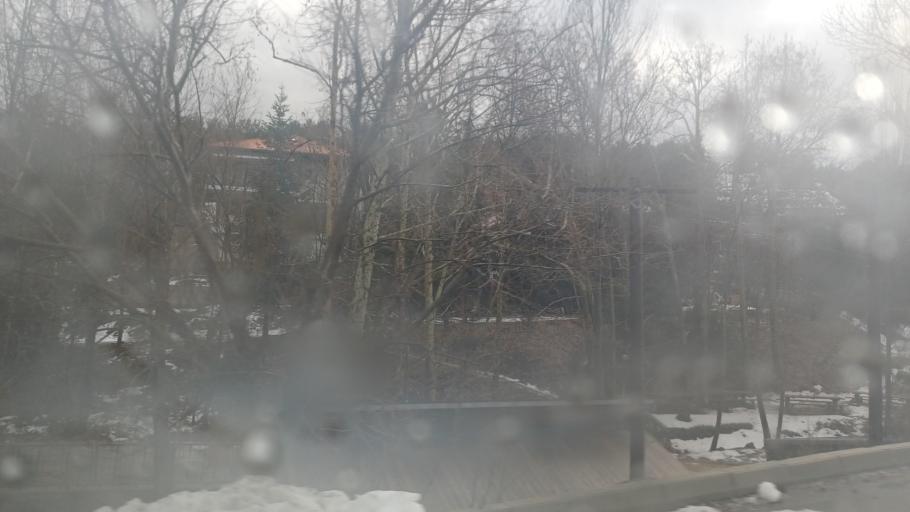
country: CY
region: Limassol
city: Kyperounta
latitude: 34.9405
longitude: 32.9633
